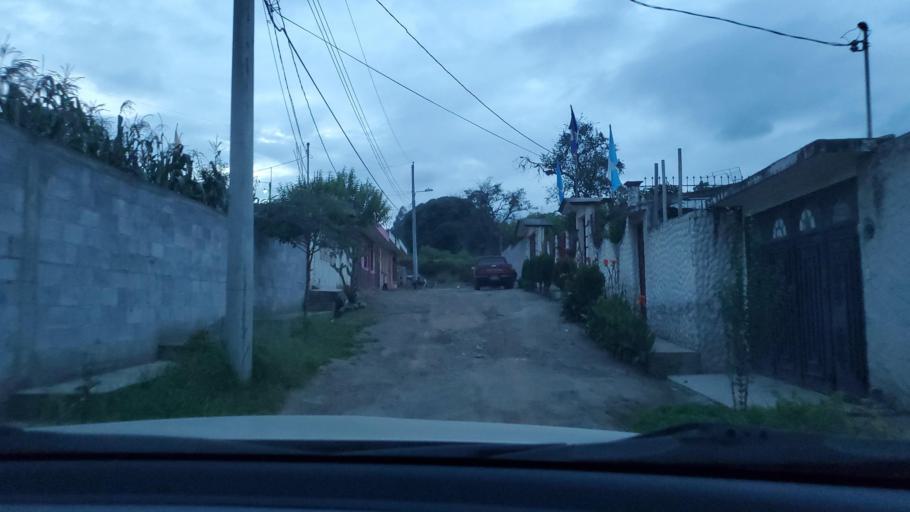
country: GT
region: Quetzaltenango
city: Quetzaltenango
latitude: 14.8255
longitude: -91.5396
